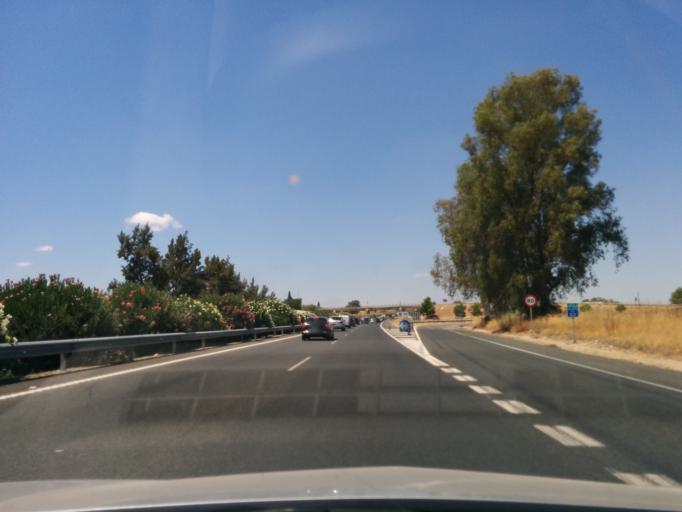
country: ES
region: Andalusia
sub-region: Provincia de Sevilla
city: Aznalcazar
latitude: 37.3620
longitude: -6.2688
